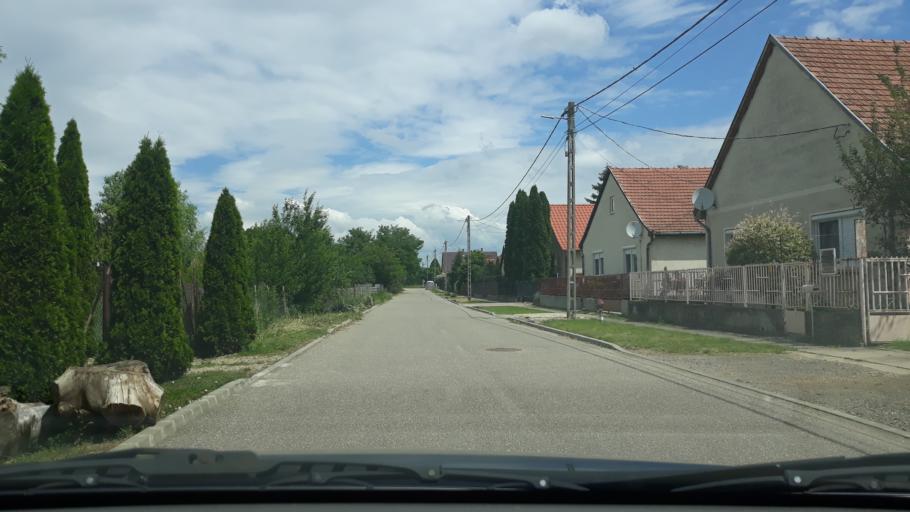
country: HU
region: Hajdu-Bihar
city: Biharkeresztes
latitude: 47.1315
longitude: 21.7330
